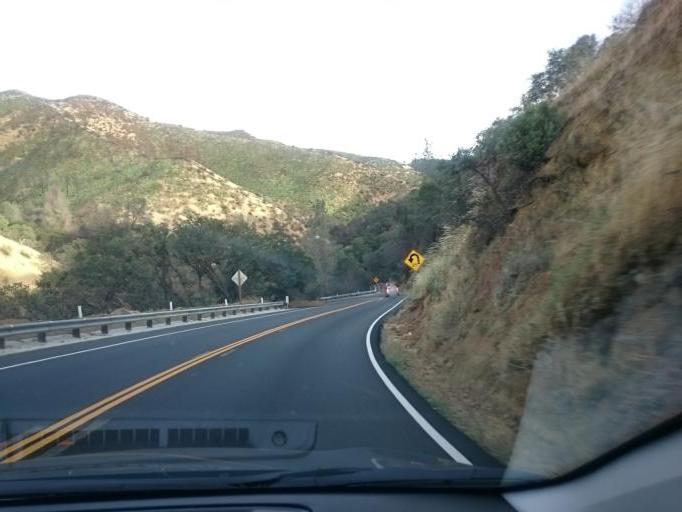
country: US
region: California
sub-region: Yolo County
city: Winters
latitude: 38.5101
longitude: -122.0981
